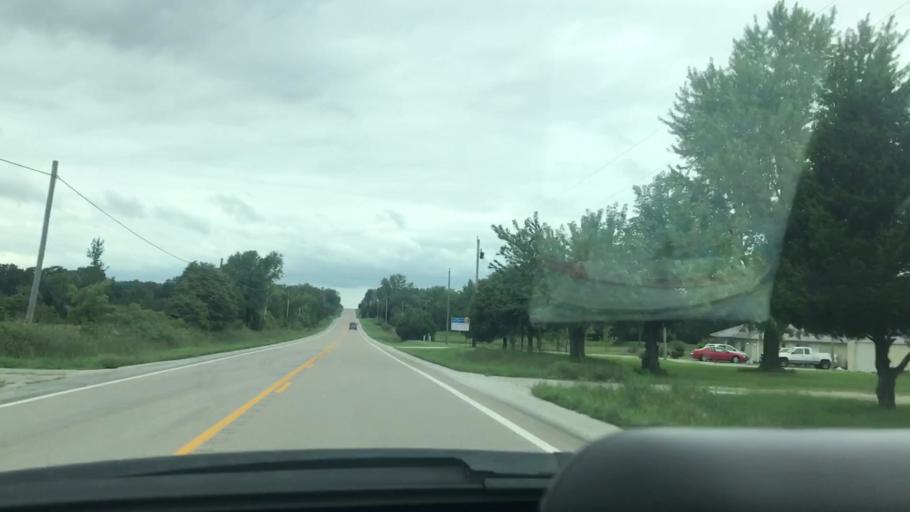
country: US
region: Missouri
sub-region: Dallas County
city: Buffalo
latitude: 37.6962
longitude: -93.1036
